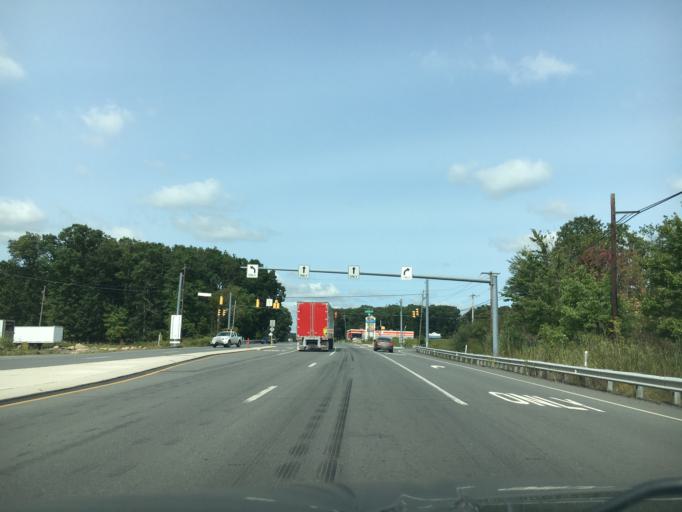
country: US
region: Pennsylvania
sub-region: Schuylkill County
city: Hometown
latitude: 40.8327
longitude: -75.9881
